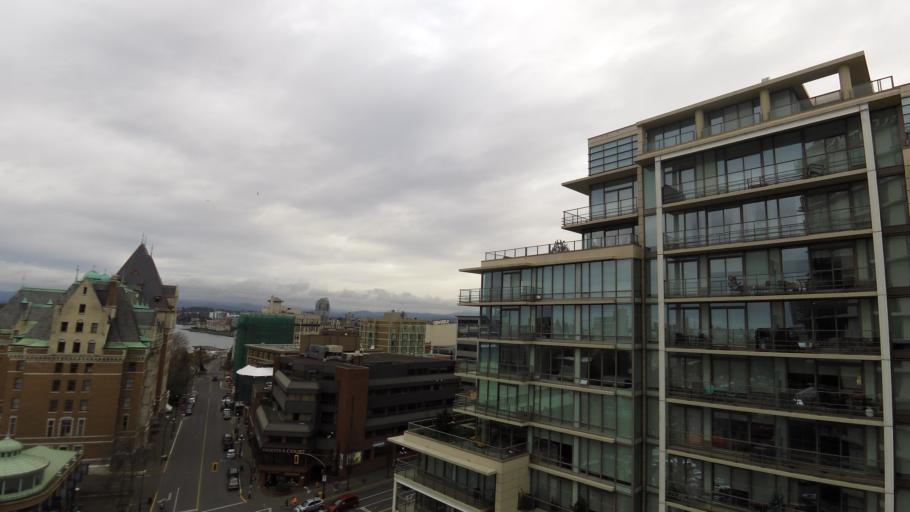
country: CA
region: British Columbia
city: Victoria
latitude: 48.4220
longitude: -123.3652
